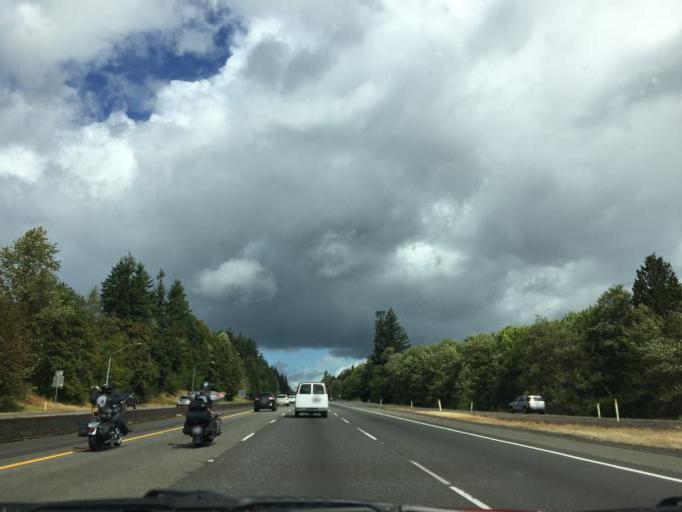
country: US
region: Washington
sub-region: Lewis County
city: Winlock
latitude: 46.4778
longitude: -122.8823
